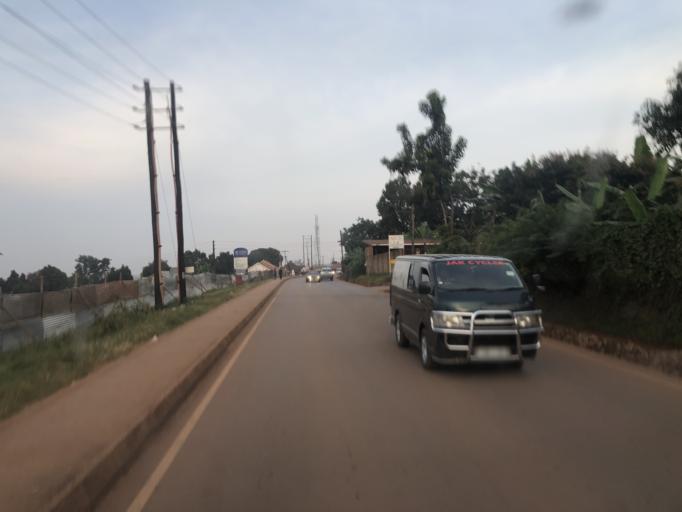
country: UG
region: Central Region
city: Kampala Central Division
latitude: 0.2925
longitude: 32.5330
